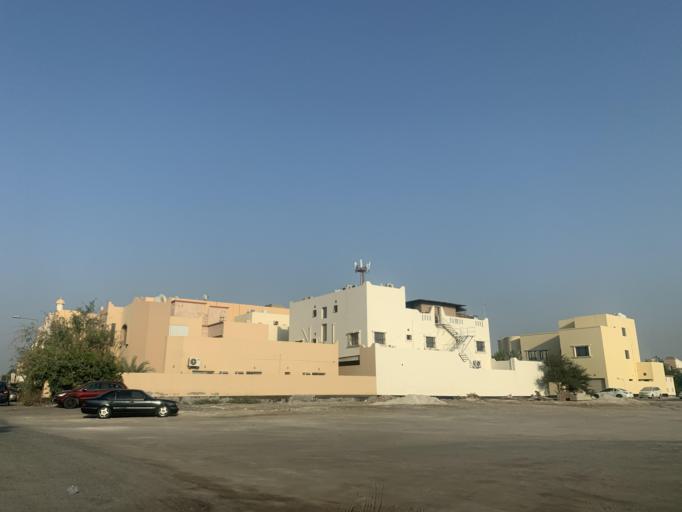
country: BH
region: Manama
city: Jidd Hafs
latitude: 26.2149
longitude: 50.5245
